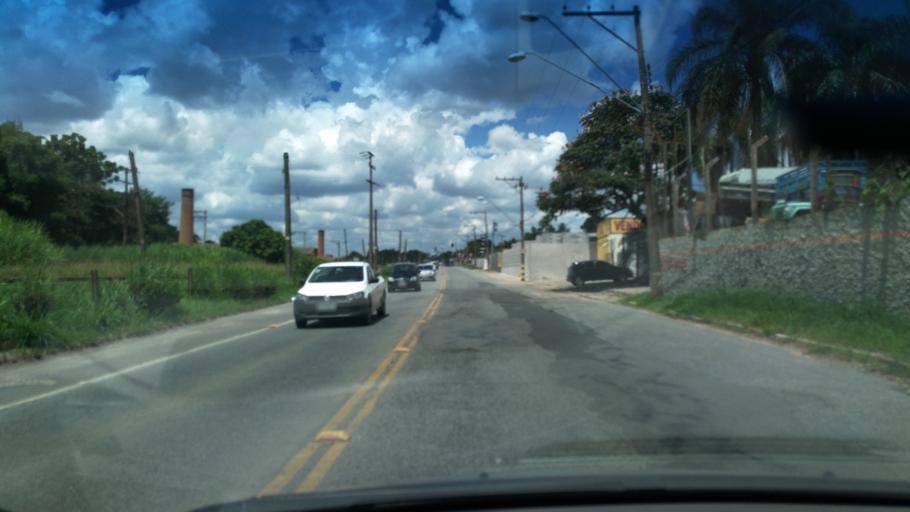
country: BR
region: Sao Paulo
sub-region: Vinhedo
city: Vinhedo
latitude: -23.0016
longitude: -46.9889
